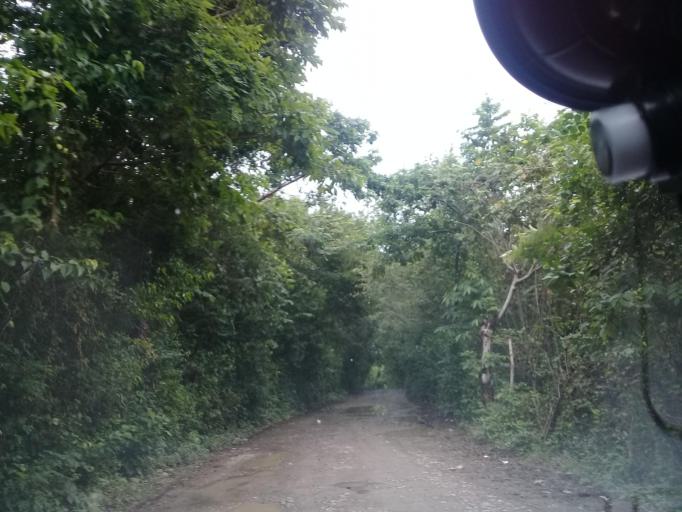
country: MX
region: Veracruz
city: Platon Sanchez
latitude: 21.2140
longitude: -98.3654
